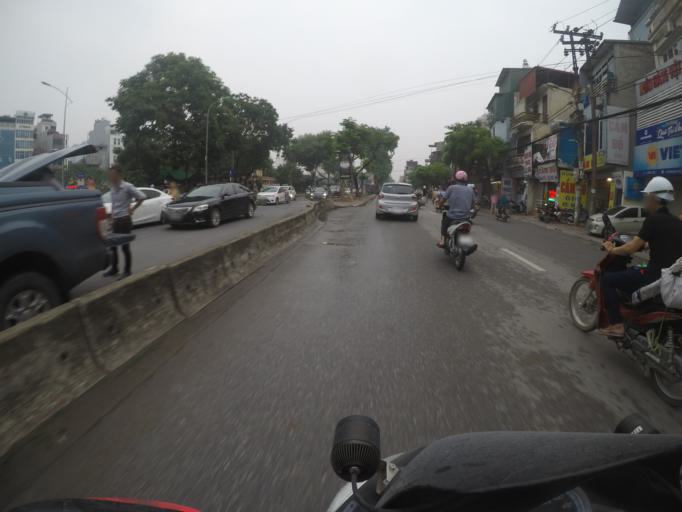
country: VN
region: Ha Noi
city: Thanh Xuan
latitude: 21.0092
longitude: 105.8139
